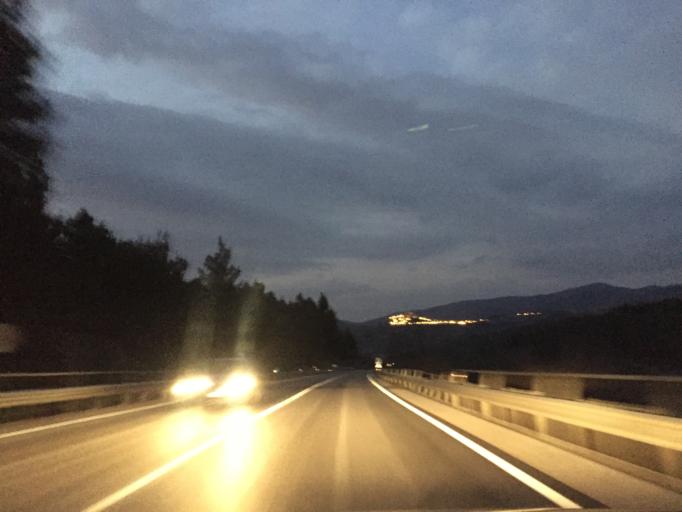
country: IT
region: Apulia
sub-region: Provincia di Foggia
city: Volturara Appula
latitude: 41.4725
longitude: 15.0542
